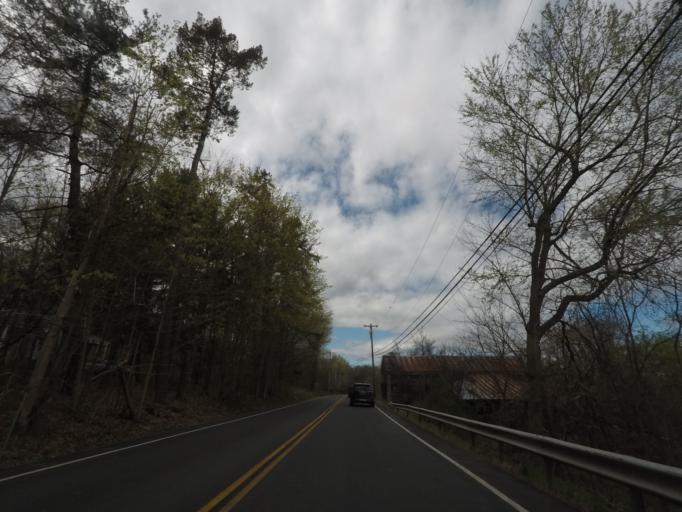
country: US
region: New York
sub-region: Columbia County
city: Valatie
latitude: 42.3838
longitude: -73.6411
